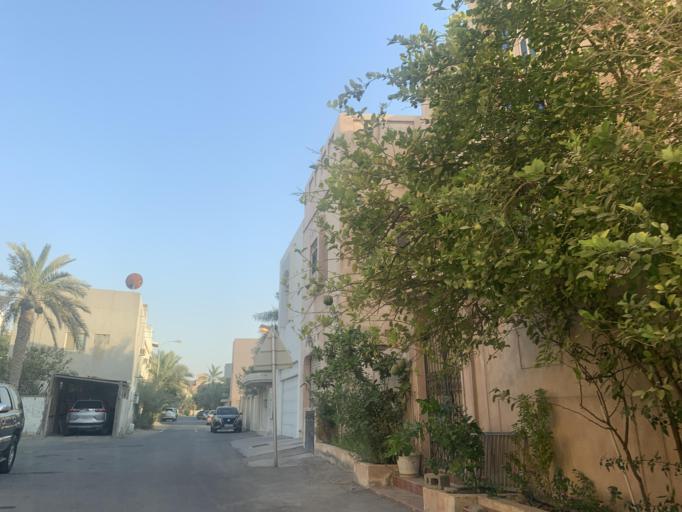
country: BH
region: Manama
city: Jidd Hafs
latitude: 26.2151
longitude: 50.5316
